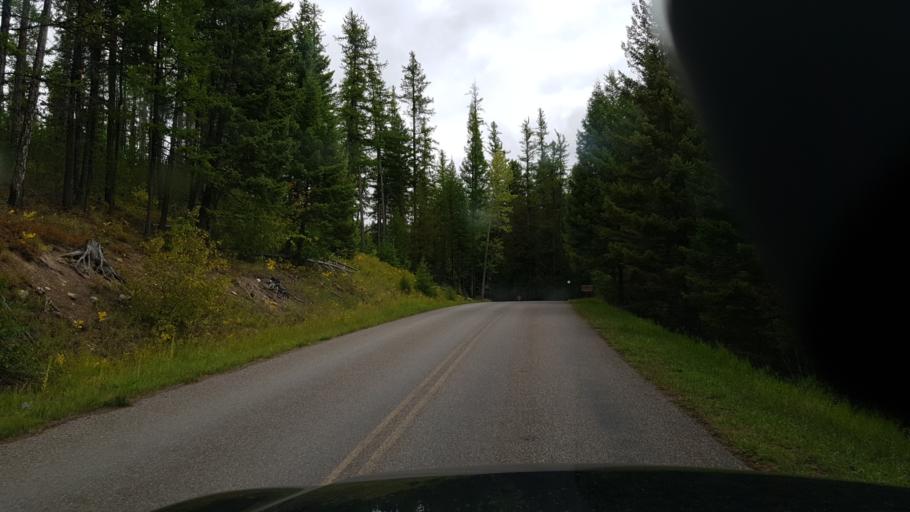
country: US
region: Montana
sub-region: Flathead County
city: Columbia Falls
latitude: 48.5456
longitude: -113.9866
